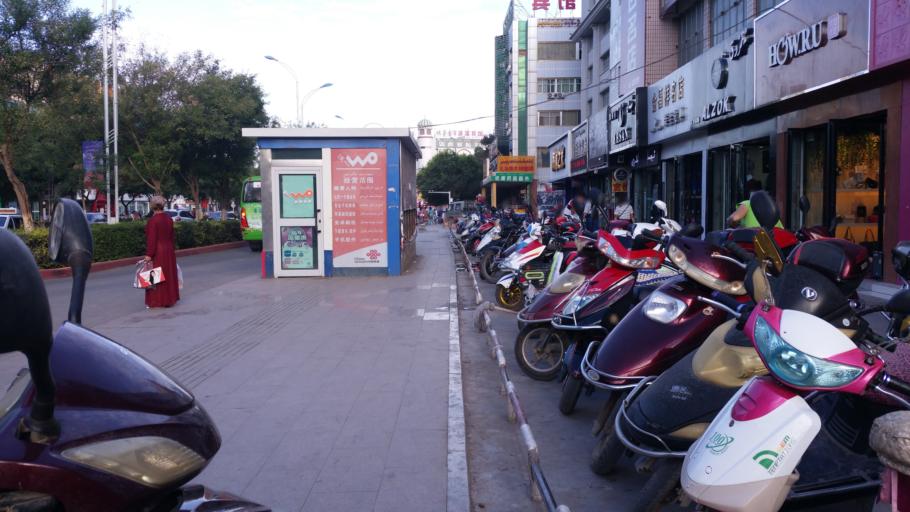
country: CN
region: Xinjiang Uygur Zizhiqu
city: Laochenglu
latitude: 42.9409
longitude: 89.1762
